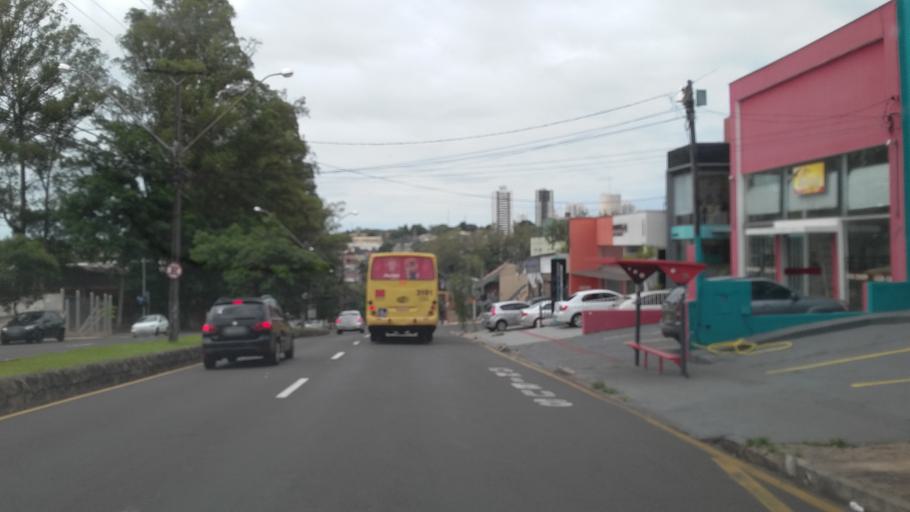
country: BR
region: Parana
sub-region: Londrina
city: Londrina
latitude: -23.3263
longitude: -51.1677
